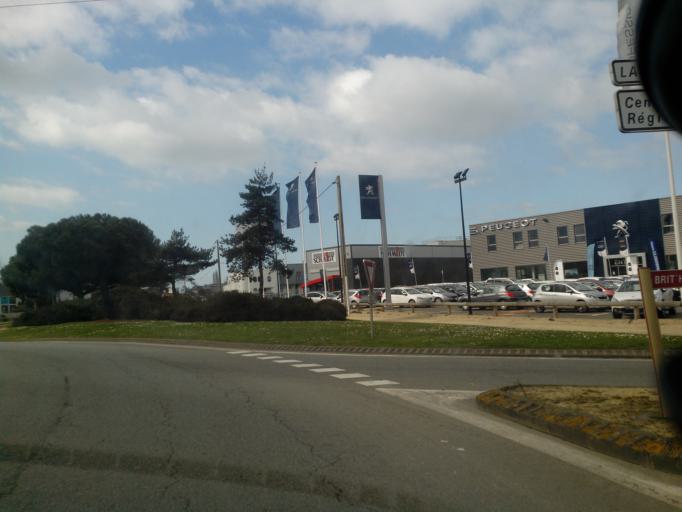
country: FR
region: Brittany
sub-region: Departement d'Ille-et-Vilaine
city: Saint-Jouan-des-Guerets
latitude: 48.6216
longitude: -1.9926
